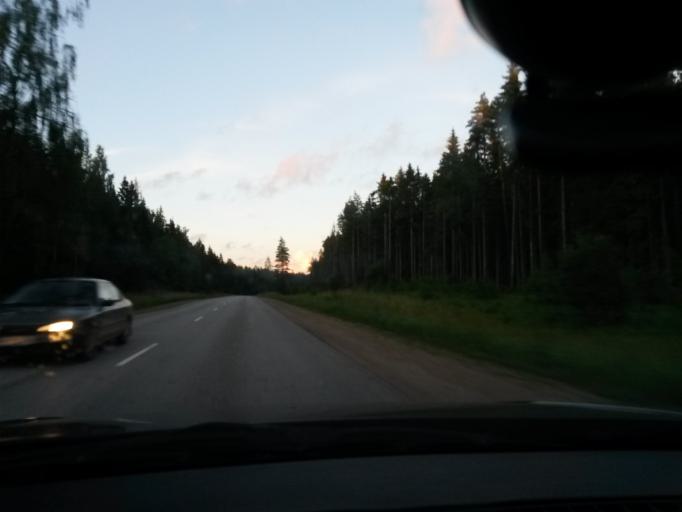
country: LV
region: Madonas Rajons
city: Madona
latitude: 56.8161
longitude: 26.1268
